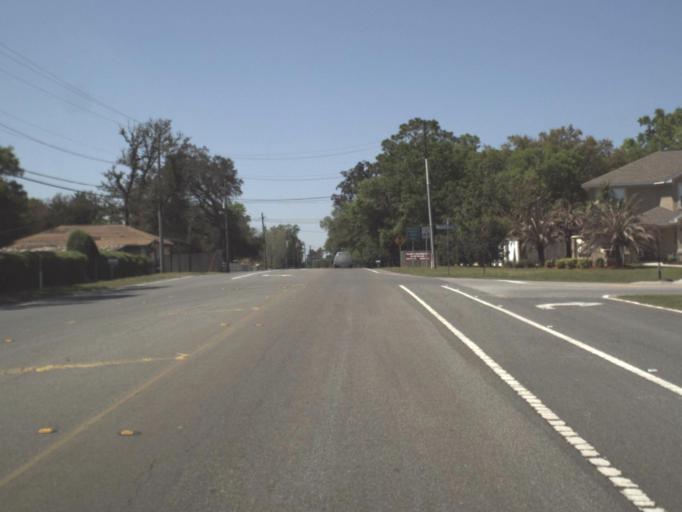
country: US
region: Florida
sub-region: Escambia County
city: Bellview
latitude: 30.4840
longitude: -87.3136
